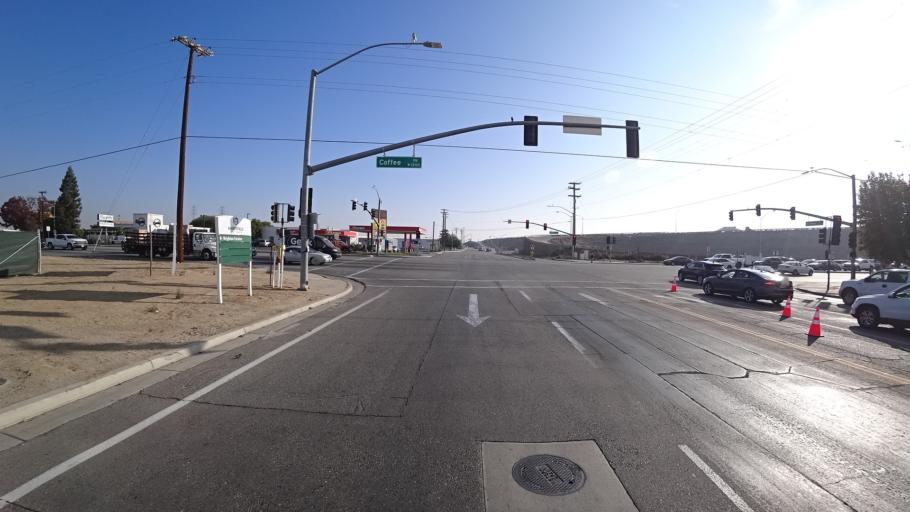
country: US
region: California
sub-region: Kern County
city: Greenacres
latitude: 35.3689
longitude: -119.0926
